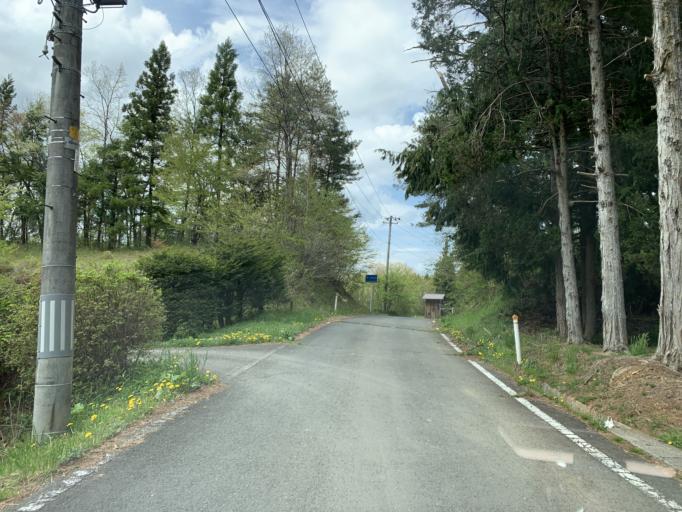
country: JP
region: Iwate
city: Ichinoseki
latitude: 38.7826
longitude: 141.4324
